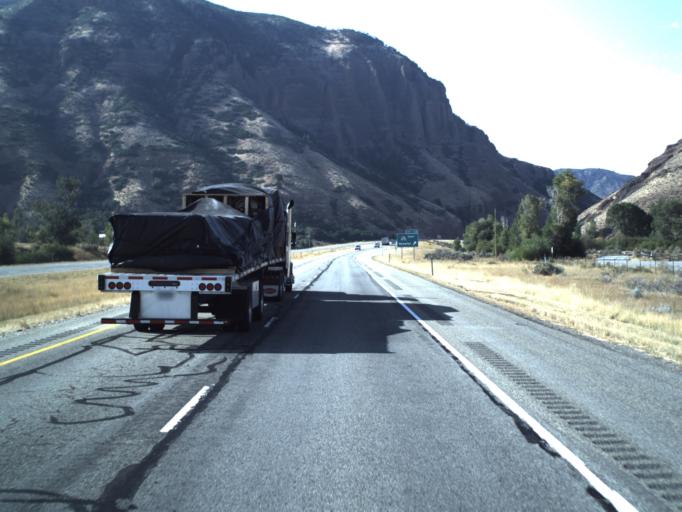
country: US
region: Utah
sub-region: Morgan County
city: Morgan
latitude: 41.0407
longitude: -111.5173
